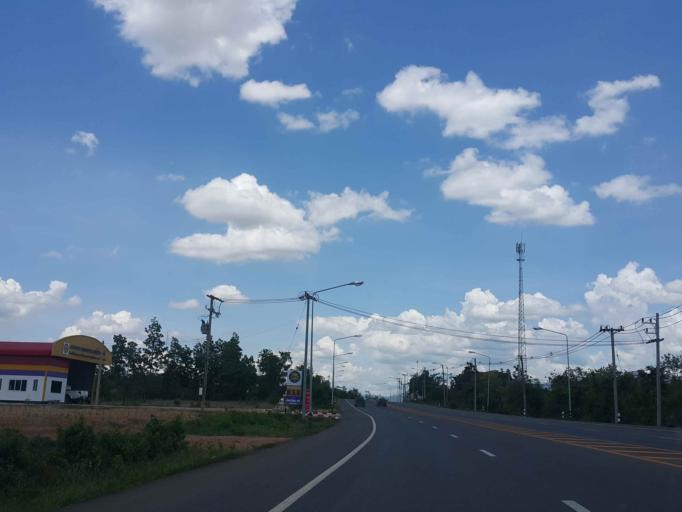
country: TH
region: Phrae
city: Nong Muang Khai
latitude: 18.2026
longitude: 100.2169
